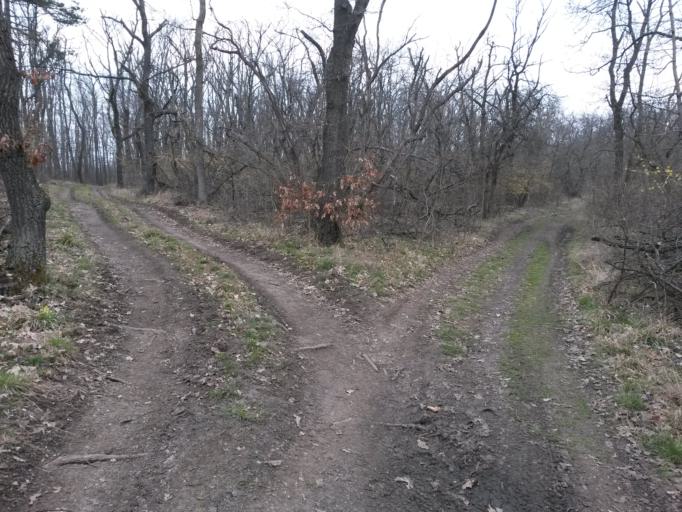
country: HU
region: Pest
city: Telki
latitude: 47.5808
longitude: 18.8458
